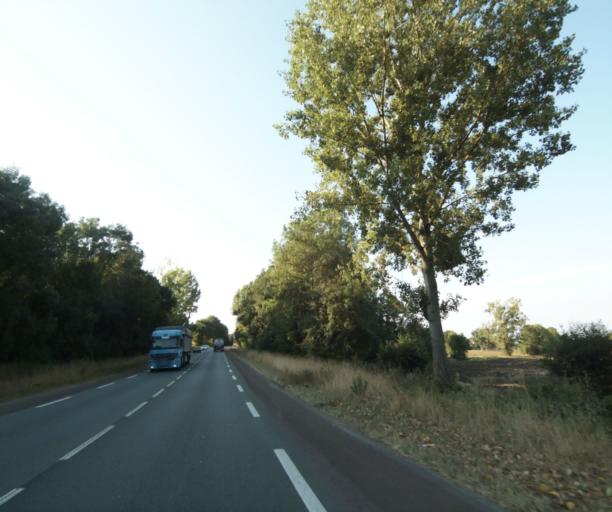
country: FR
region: Poitou-Charentes
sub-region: Departement de la Charente-Maritime
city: Cabariot
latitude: 45.9410
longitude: -0.8642
